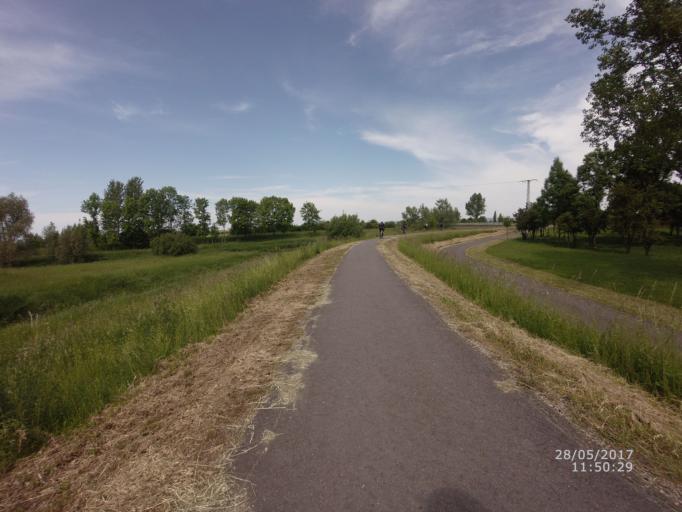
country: DE
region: Thuringia
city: Griefstedt
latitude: 51.2043
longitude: 11.1417
